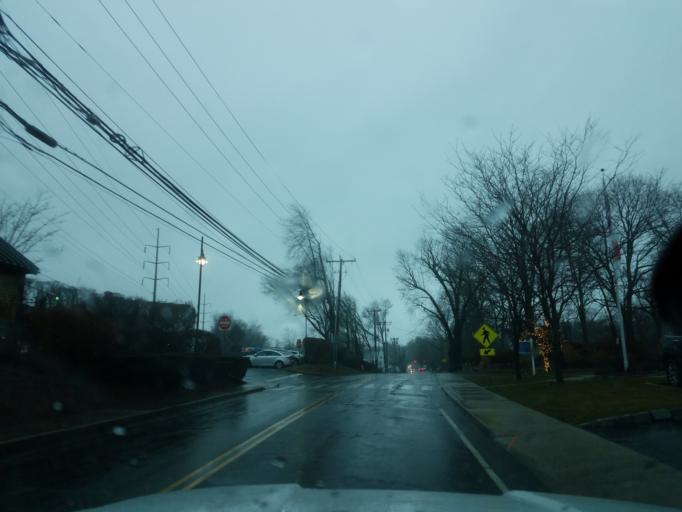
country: US
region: Connecticut
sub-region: Fairfield County
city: Darien
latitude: 41.0774
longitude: -73.4708
